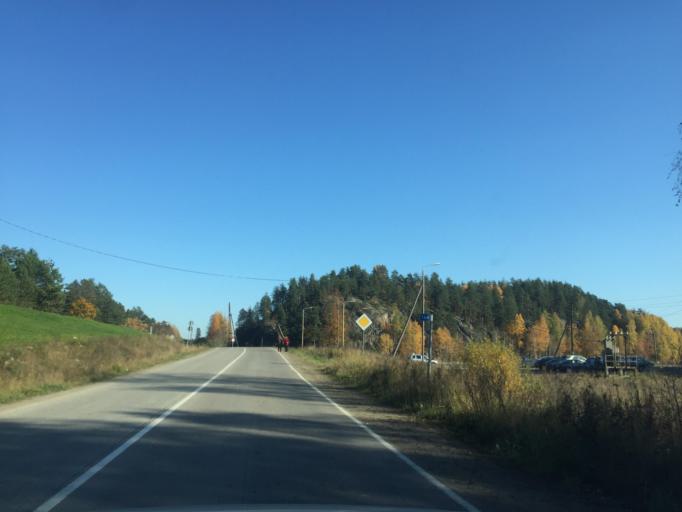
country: RU
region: Leningrad
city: Kuznechnoye
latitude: 61.2991
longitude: 29.9073
